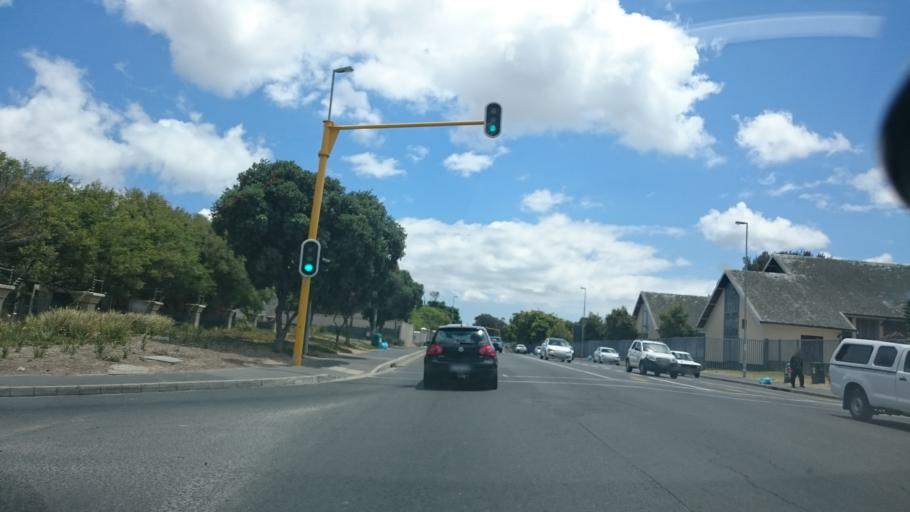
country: ZA
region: Western Cape
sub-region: City of Cape Town
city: Bergvliet
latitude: -34.0624
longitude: 18.4595
